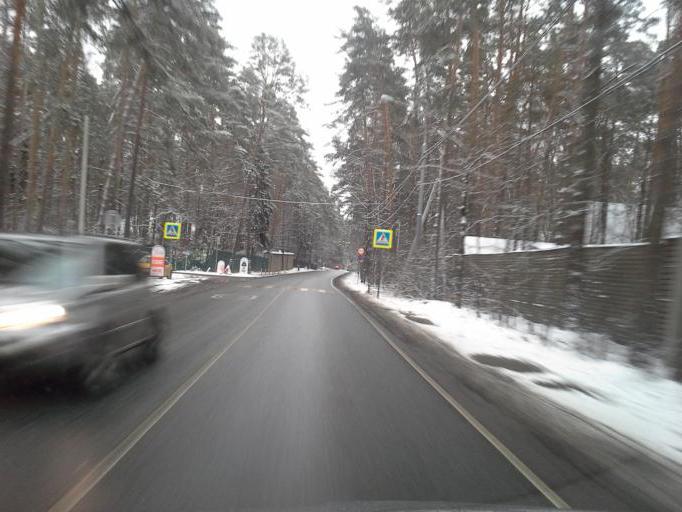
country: RU
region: Moskovskaya
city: Nikolina Gora
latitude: 55.7318
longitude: 37.0450
